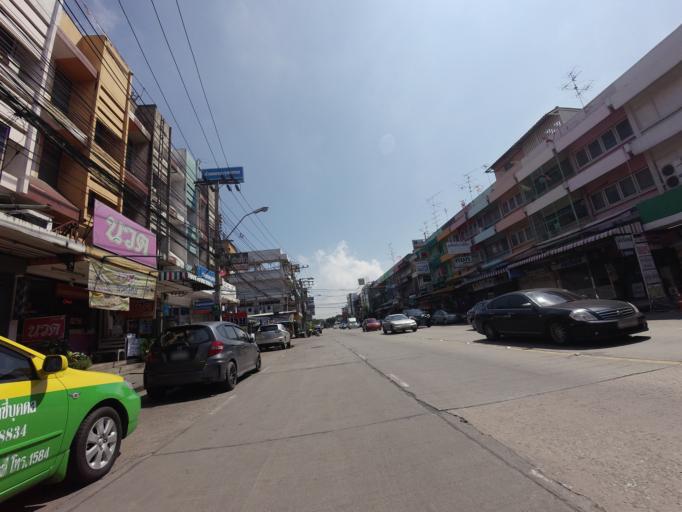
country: TH
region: Bangkok
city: Bang Kapi
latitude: 13.7803
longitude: 100.6435
